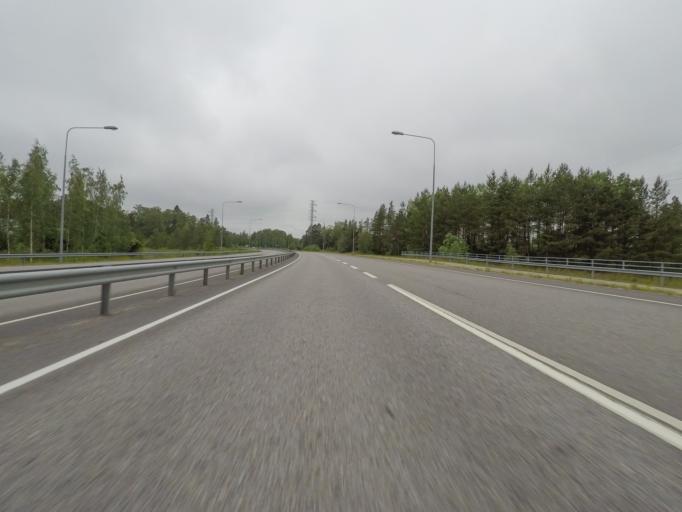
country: FI
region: Varsinais-Suomi
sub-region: Turku
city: Naantali
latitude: 60.4748
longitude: 22.0636
